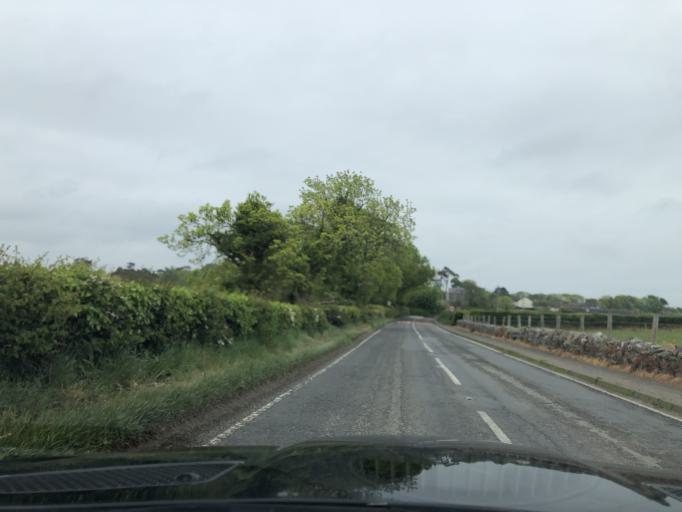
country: GB
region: Northern Ireland
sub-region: Down District
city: Portaferry
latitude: 54.3661
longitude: -5.5630
